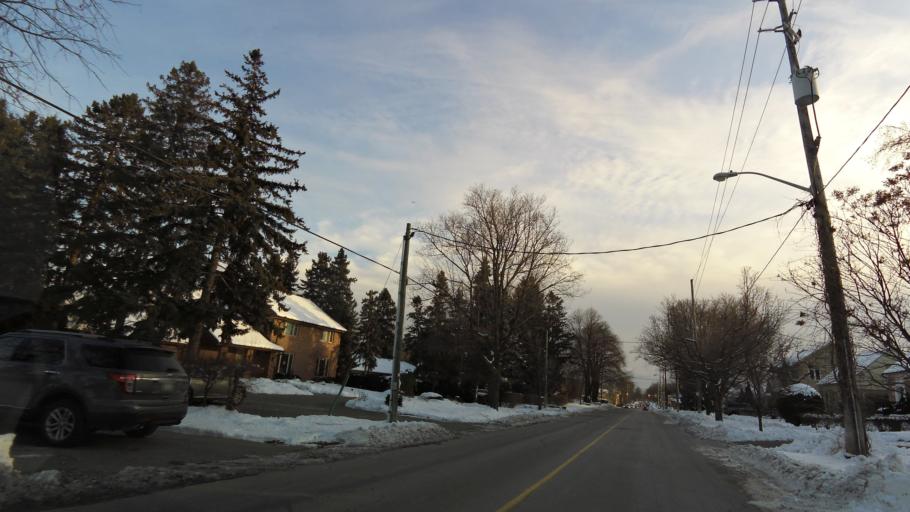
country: CA
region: Ontario
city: Etobicoke
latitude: 43.6506
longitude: -79.5498
